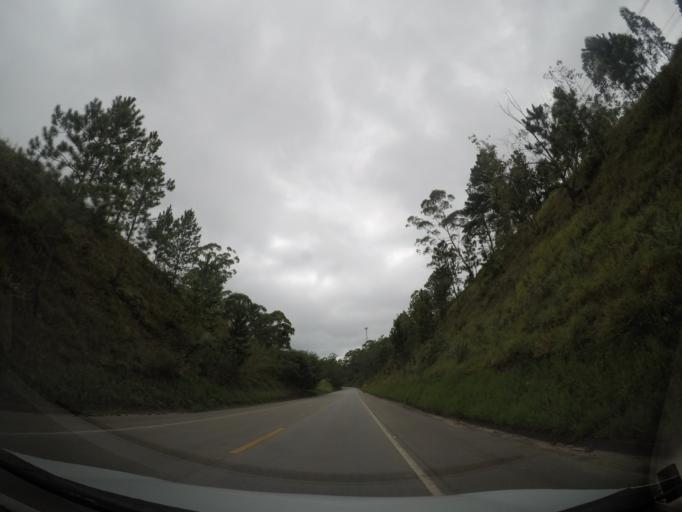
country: BR
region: Sao Paulo
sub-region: Aruja
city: Aruja
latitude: -23.3579
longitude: -46.4166
